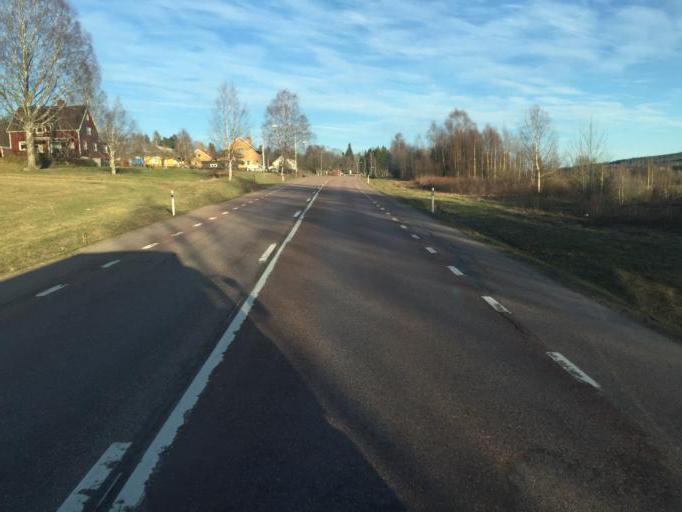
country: SE
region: Dalarna
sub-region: Borlange Kommun
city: Borlaenge
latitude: 60.5352
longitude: 15.2957
